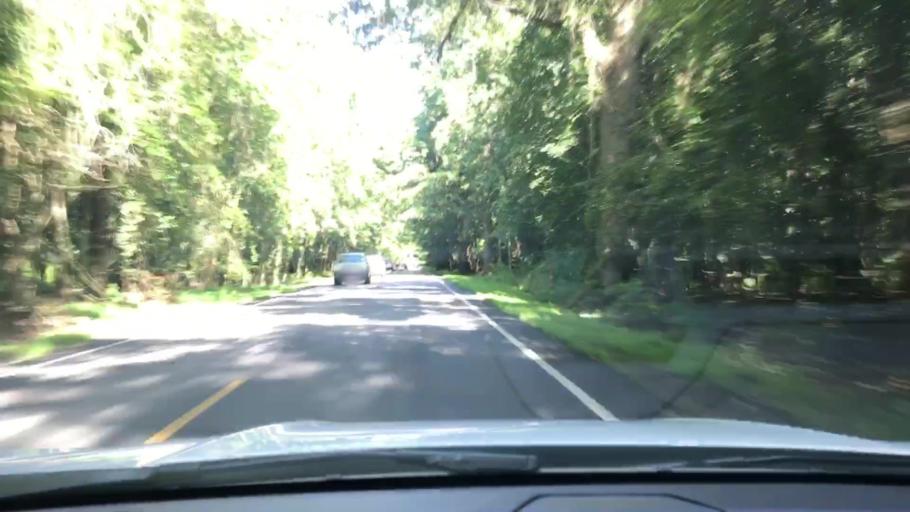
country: US
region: South Carolina
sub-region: Berkeley County
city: Hanahan
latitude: 32.8740
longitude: -80.0938
